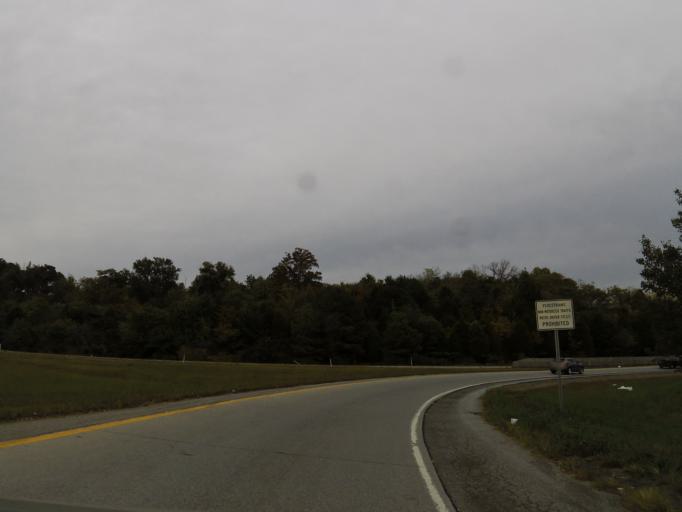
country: US
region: Tennessee
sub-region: Blount County
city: Alcoa
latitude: 35.8369
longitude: -83.9702
